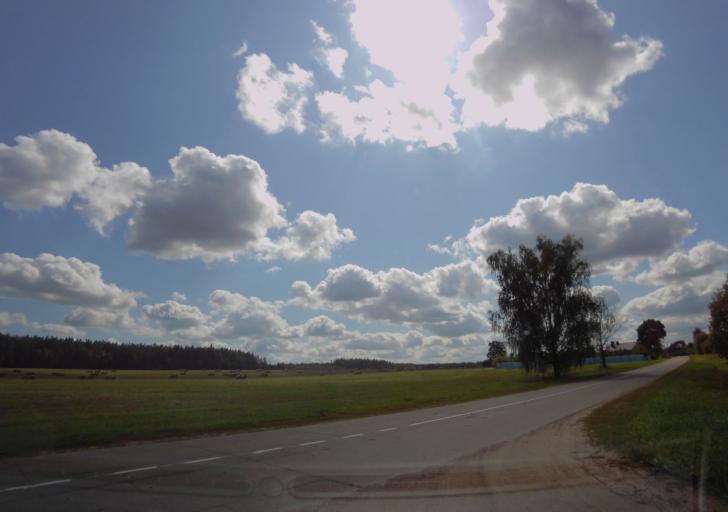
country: BY
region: Minsk
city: Horad Barysaw
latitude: 54.3639
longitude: 28.4681
